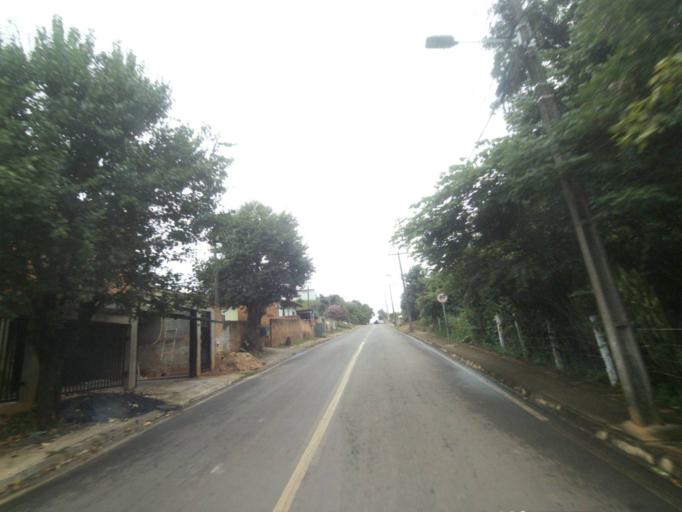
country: BR
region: Parana
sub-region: Telemaco Borba
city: Telemaco Borba
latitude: -24.3209
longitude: -50.6542
